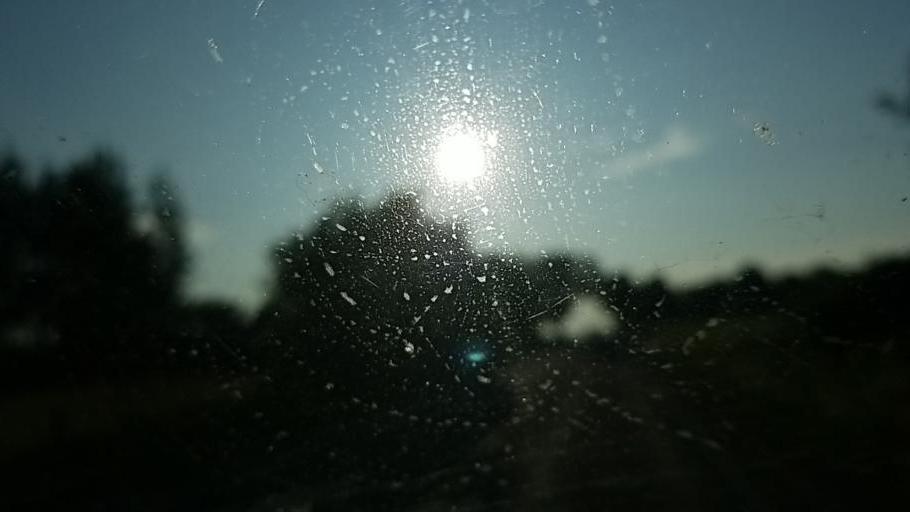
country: US
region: Michigan
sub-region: Montcalm County
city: Greenville
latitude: 43.2499
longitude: -85.2216
